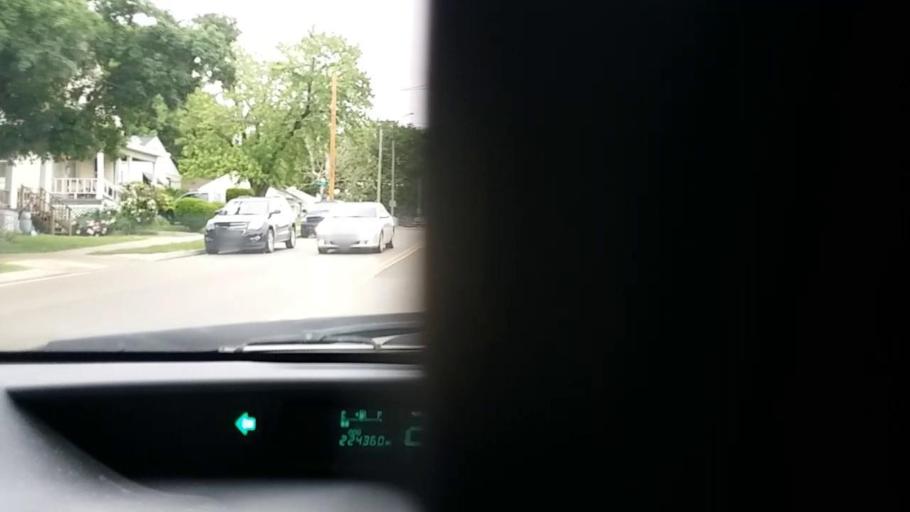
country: US
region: Illinois
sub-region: Peoria County
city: North Peoria
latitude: 40.7104
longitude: -89.6009
